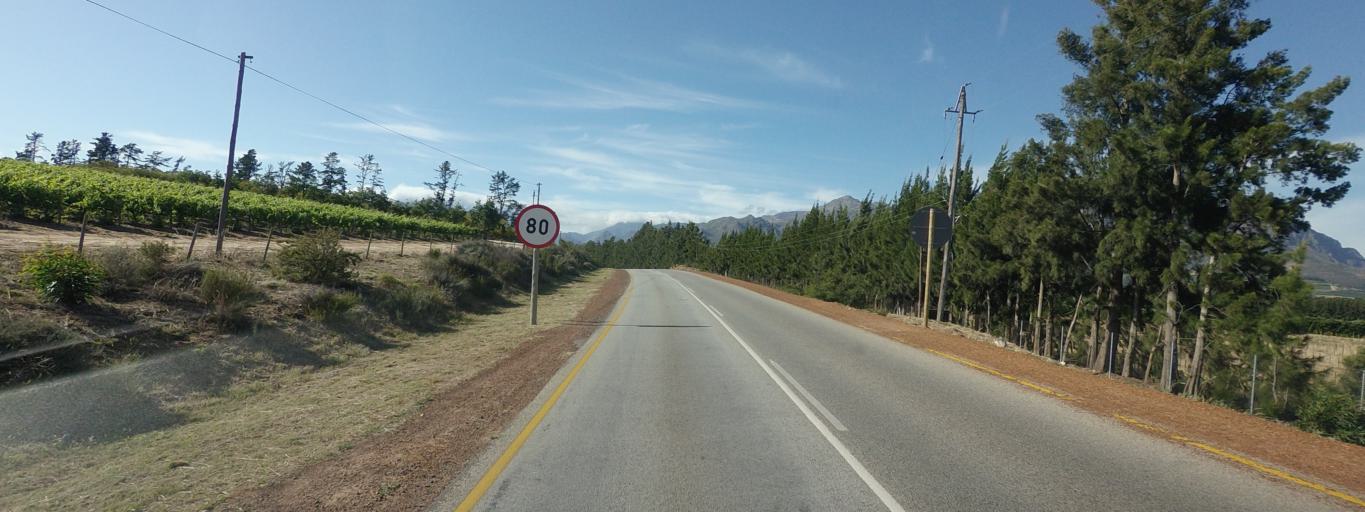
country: ZA
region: Western Cape
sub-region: Cape Winelands District Municipality
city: Paarl
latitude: -33.8624
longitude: 19.0395
